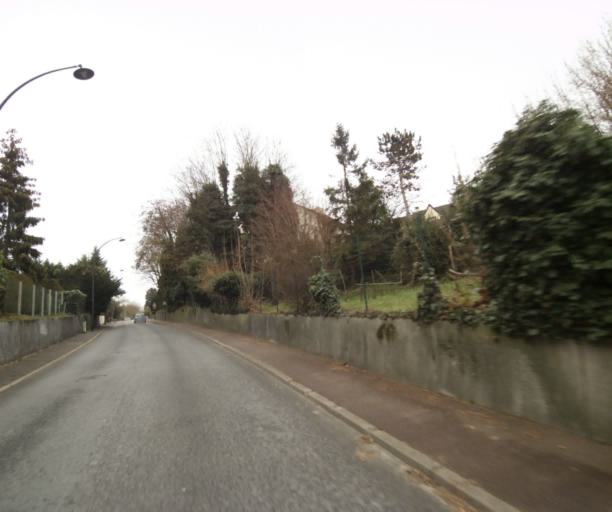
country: FR
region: Ile-de-France
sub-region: Departement des Hauts-de-Seine
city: Rueil-Malmaison
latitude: 48.8668
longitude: 2.1863
